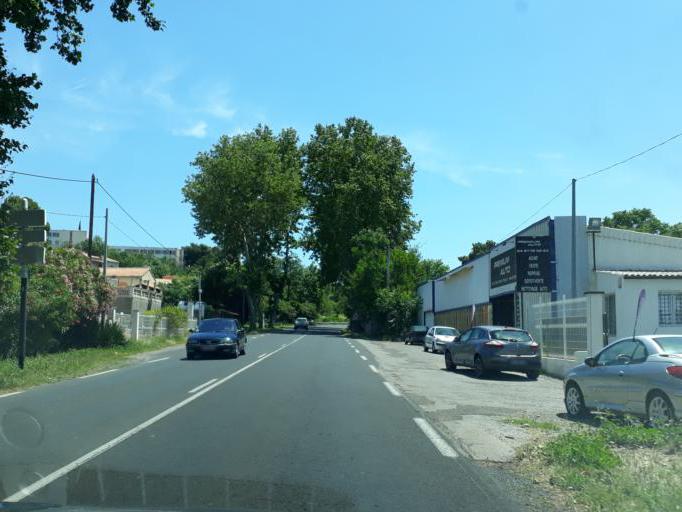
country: FR
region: Languedoc-Roussillon
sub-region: Departement de l'Herault
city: Beziers
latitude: 43.3270
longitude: 3.2448
